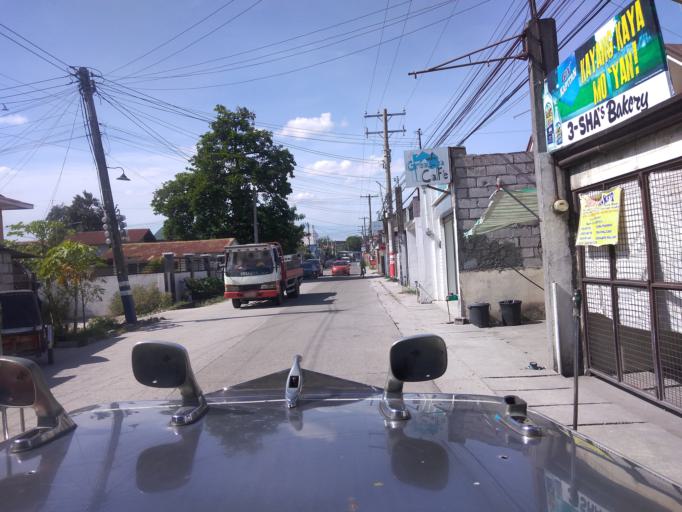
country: PH
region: Central Luzon
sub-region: Province of Pampanga
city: Magliman
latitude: 15.0370
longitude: 120.6619
